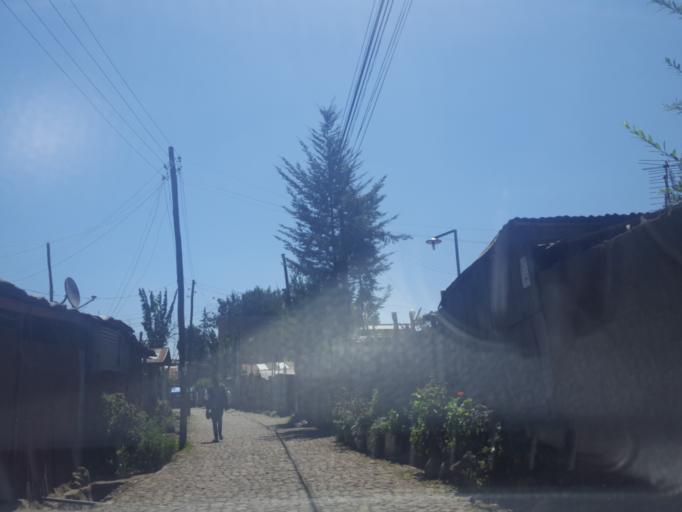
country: ET
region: Adis Abeba
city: Addis Ababa
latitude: 9.0513
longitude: 38.7605
